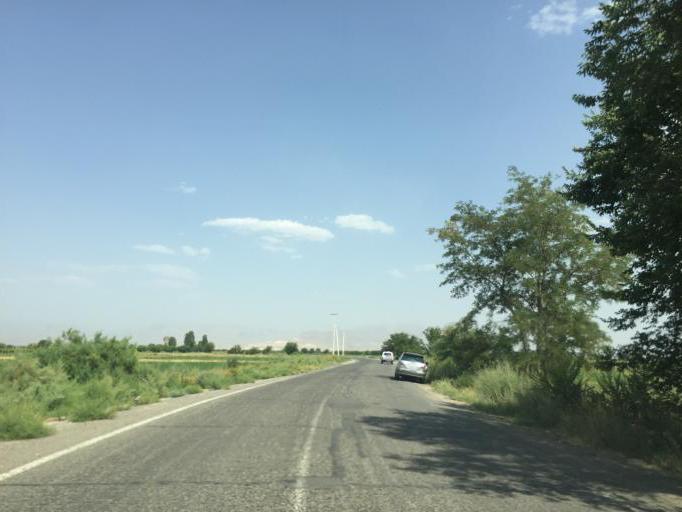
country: AM
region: Ararat
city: Shahumyan
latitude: 39.8830
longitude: 44.5824
